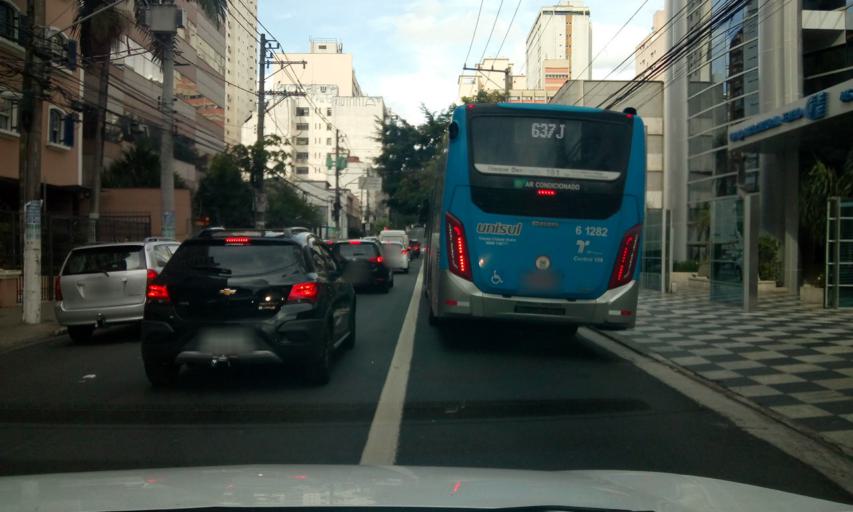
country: BR
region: Sao Paulo
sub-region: Sao Paulo
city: Sao Paulo
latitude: -23.5830
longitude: -46.6752
